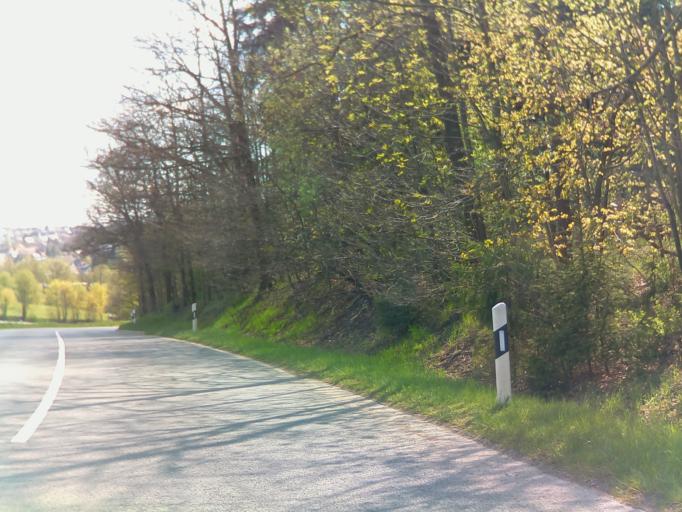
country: DE
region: Saxony
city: Neuensalz
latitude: 50.5007
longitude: 12.1859
